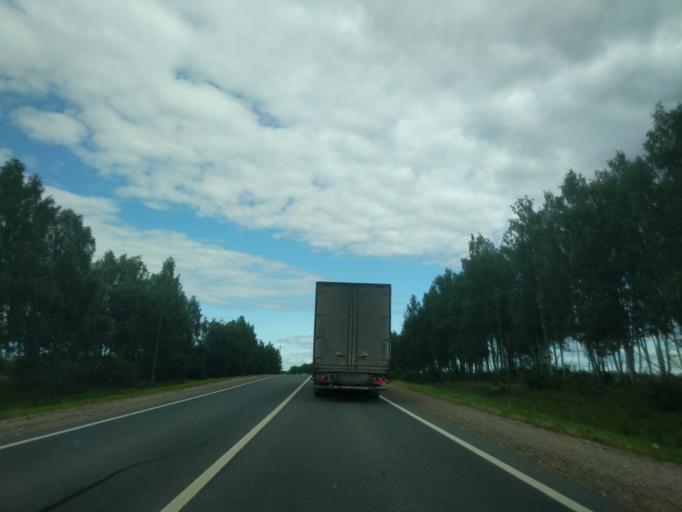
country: RU
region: Kostroma
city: Ostrovskoye
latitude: 57.8150
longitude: 42.2174
